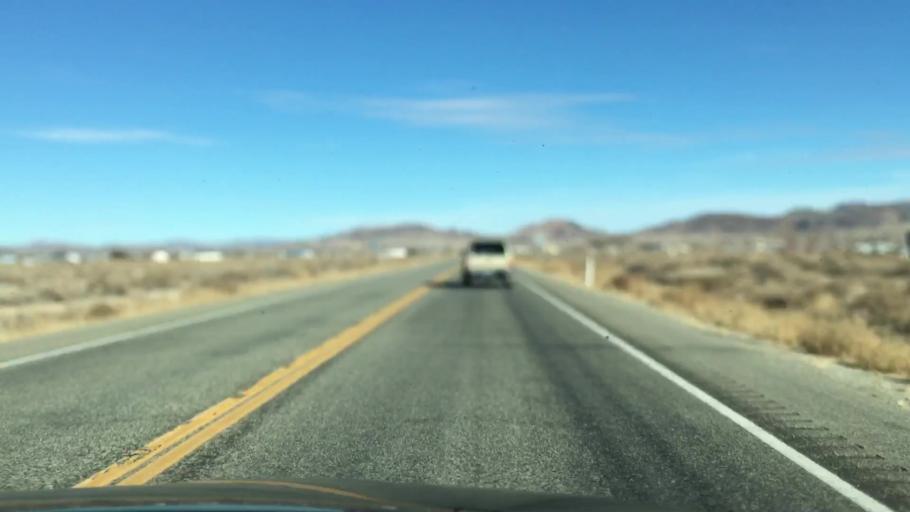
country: US
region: Nevada
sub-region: Lyon County
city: Yerington
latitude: 39.0058
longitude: -119.0867
